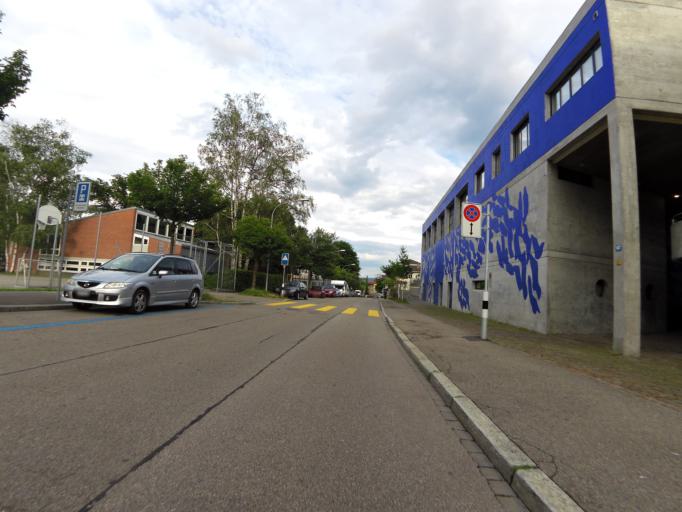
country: CH
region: Zurich
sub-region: Bezirk Zuerich
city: Zuerich (Kreis 9)
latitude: 47.3886
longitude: 8.4727
